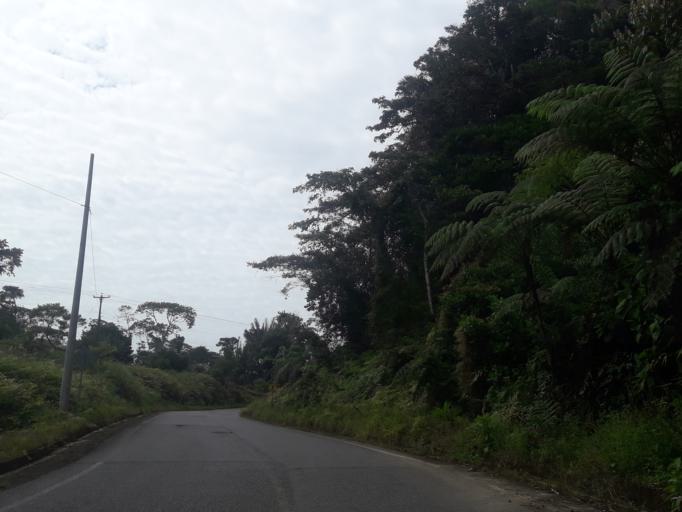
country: EC
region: Napo
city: Tena
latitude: -1.0518
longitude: -77.8965
